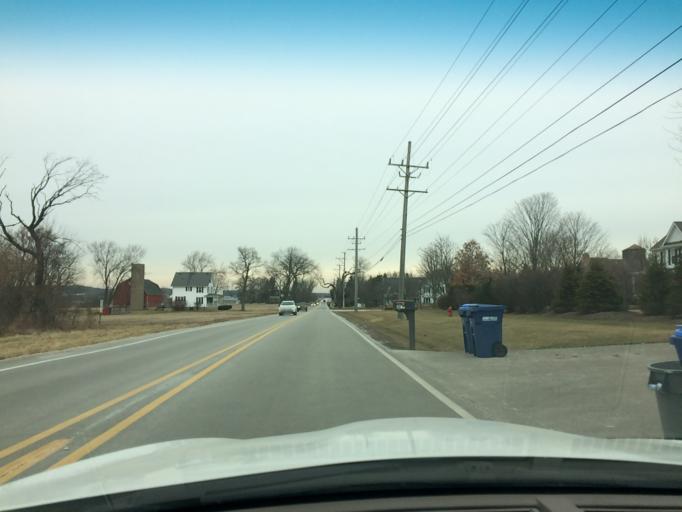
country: US
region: Illinois
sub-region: Kane County
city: Geneva
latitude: 41.8867
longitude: -88.3598
